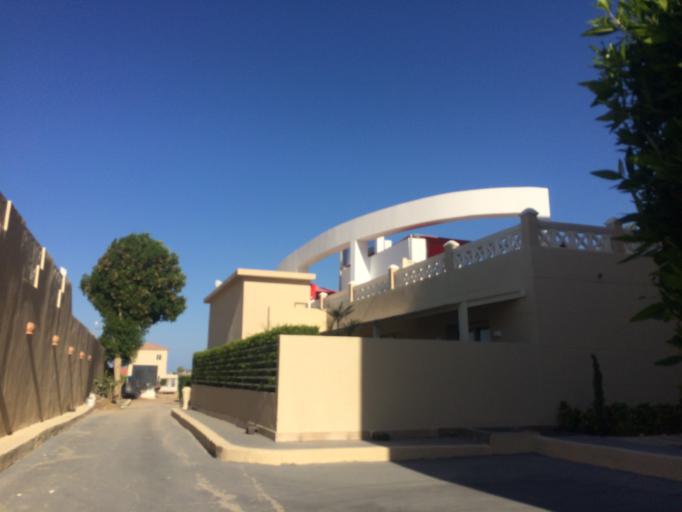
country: EG
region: Red Sea
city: Hurghada
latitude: 27.1232
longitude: 33.8291
